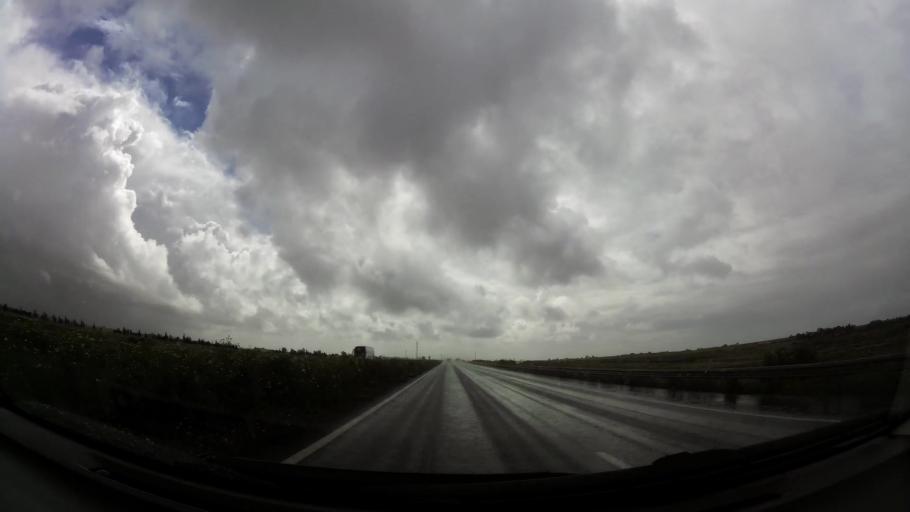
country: MA
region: Grand Casablanca
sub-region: Nouaceur
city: Dar Bouazza
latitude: 33.3939
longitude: -7.8551
